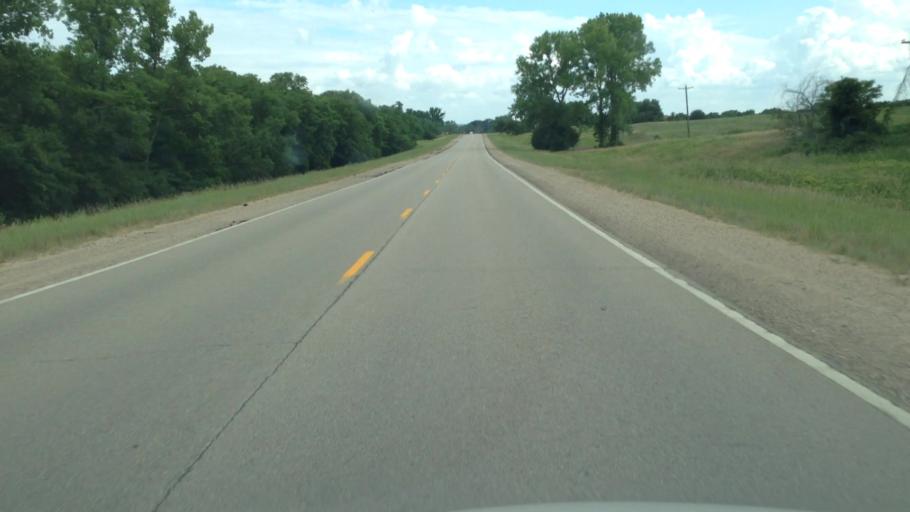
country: US
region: Kansas
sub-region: Jefferson County
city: Oskaloosa
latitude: 39.1110
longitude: -95.4837
